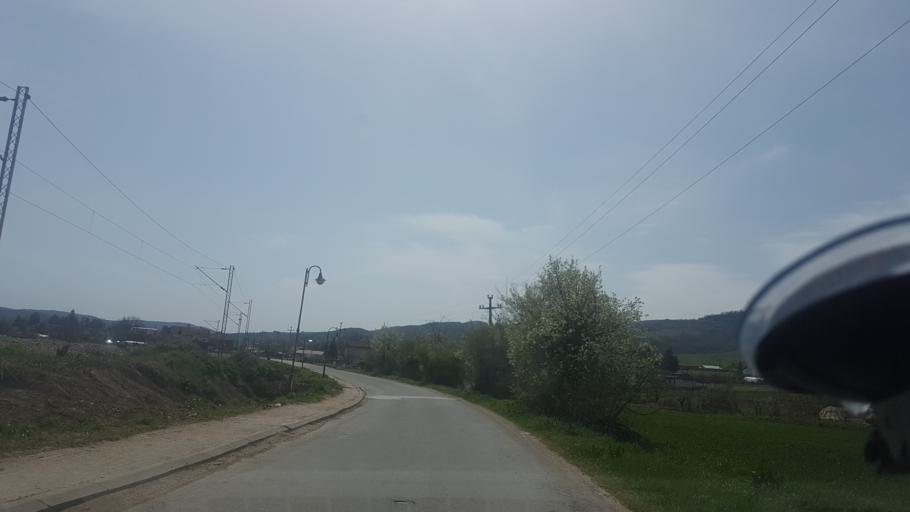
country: MK
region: Zelenikovo
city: Zelenikovo
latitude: 41.8853
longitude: 21.5879
